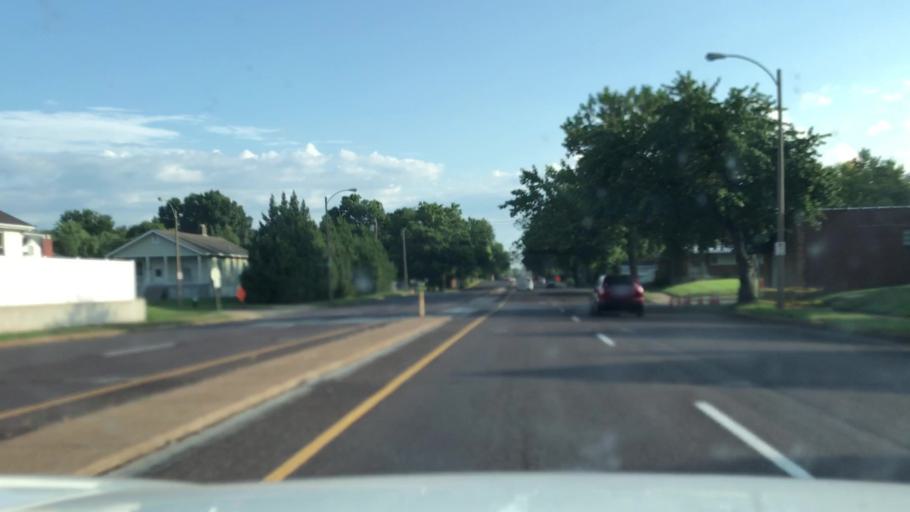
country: US
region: Missouri
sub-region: Saint Louis County
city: Maplewood
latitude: 38.5989
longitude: -90.3084
